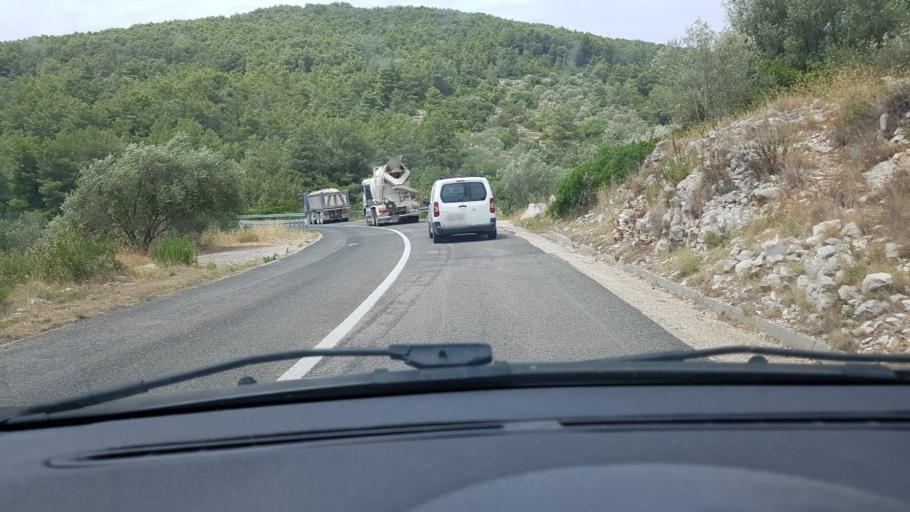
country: HR
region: Dubrovacko-Neretvanska
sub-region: Grad Dubrovnik
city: Vela Luka
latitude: 42.9507
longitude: 16.7845
